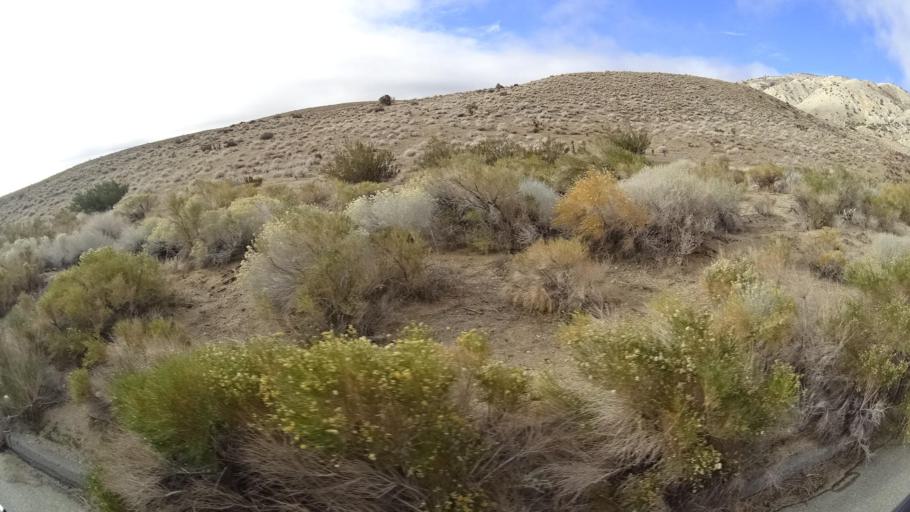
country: US
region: California
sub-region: Kern County
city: Tehachapi
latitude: 35.0113
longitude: -118.3425
